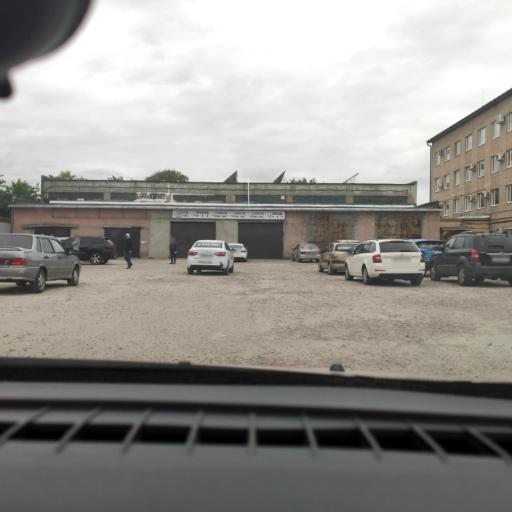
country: RU
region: Voronezj
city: Voronezh
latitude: 51.6509
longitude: 39.2868
